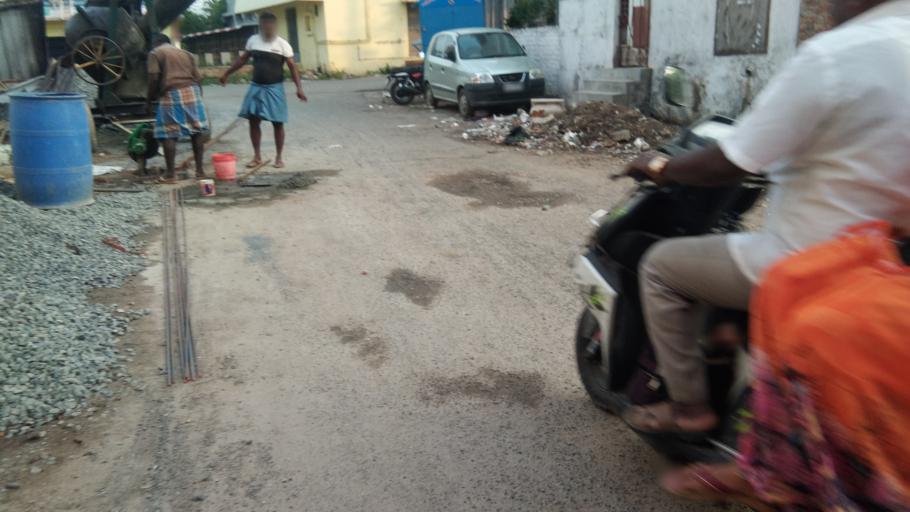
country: IN
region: Tamil Nadu
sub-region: Kancheepuram
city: Pallavaram
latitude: 12.9646
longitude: 80.1425
